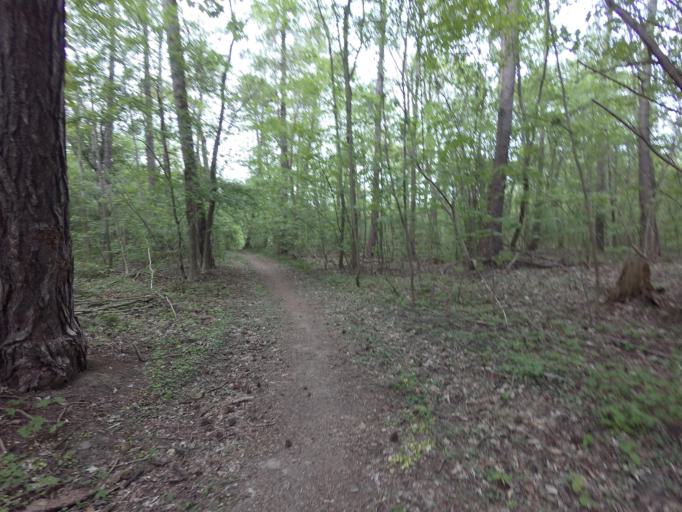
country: DE
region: Lower Saxony
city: Diekholzen
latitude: 52.1380
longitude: 9.9045
